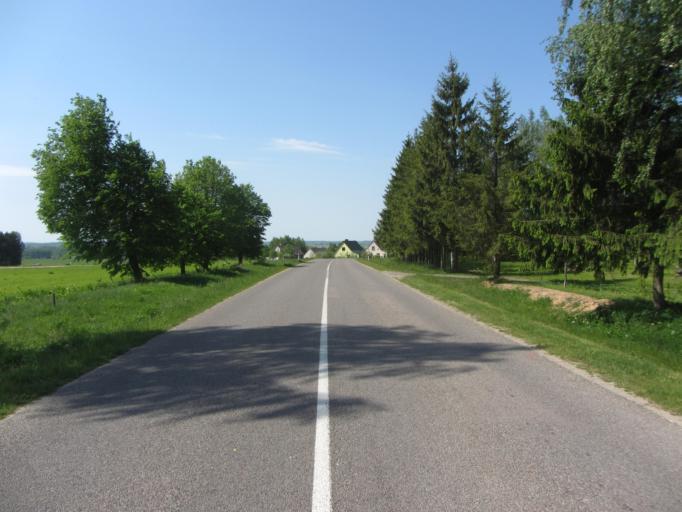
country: LT
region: Utenos apskritis
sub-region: Utena
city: Utena
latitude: 55.6126
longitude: 25.4055
